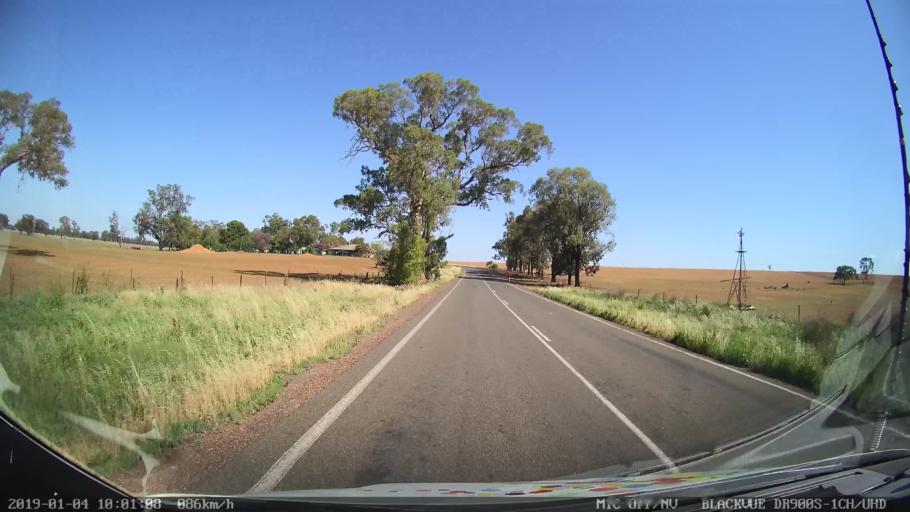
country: AU
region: New South Wales
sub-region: Cabonne
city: Canowindra
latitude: -33.4898
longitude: 148.3738
